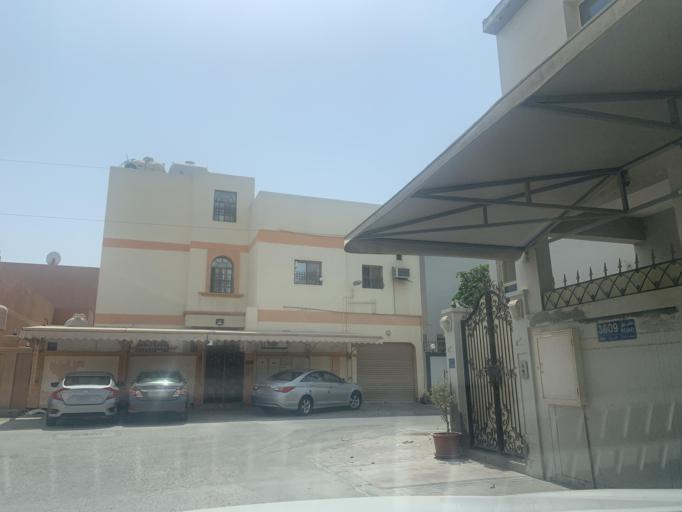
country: BH
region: Manama
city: Jidd Hafs
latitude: 26.2208
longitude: 50.4690
